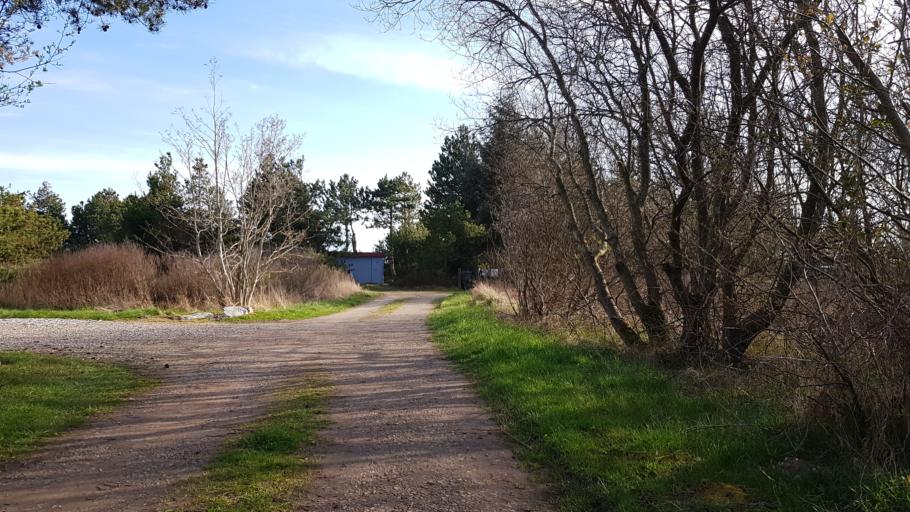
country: DE
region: Schleswig-Holstein
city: List
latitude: 55.1290
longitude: 8.5232
